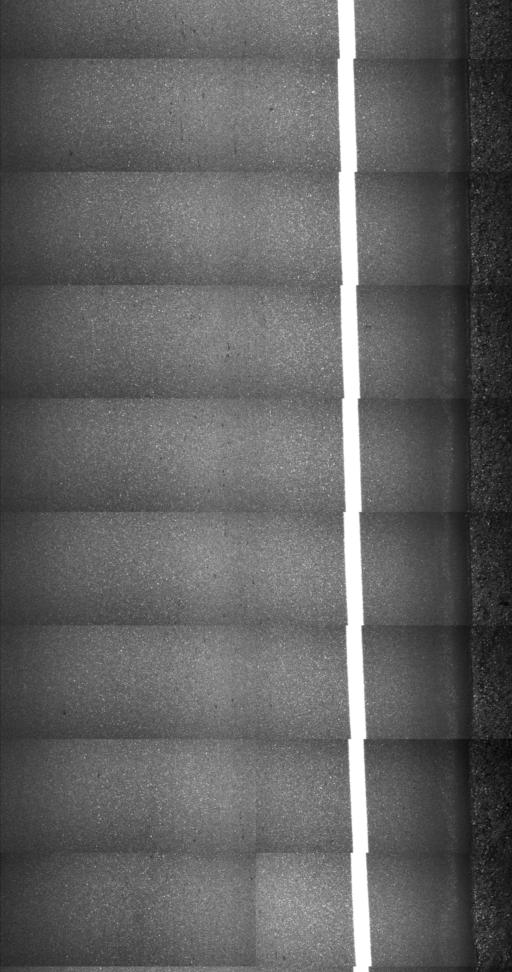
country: US
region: Vermont
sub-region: Windham County
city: Dover
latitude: 43.0589
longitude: -72.8603
